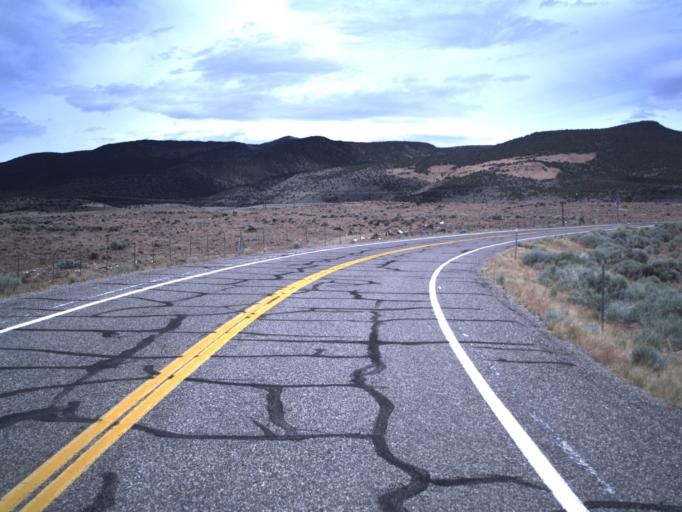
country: US
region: Utah
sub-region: Sevier County
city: Monroe
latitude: 38.6253
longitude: -112.2275
